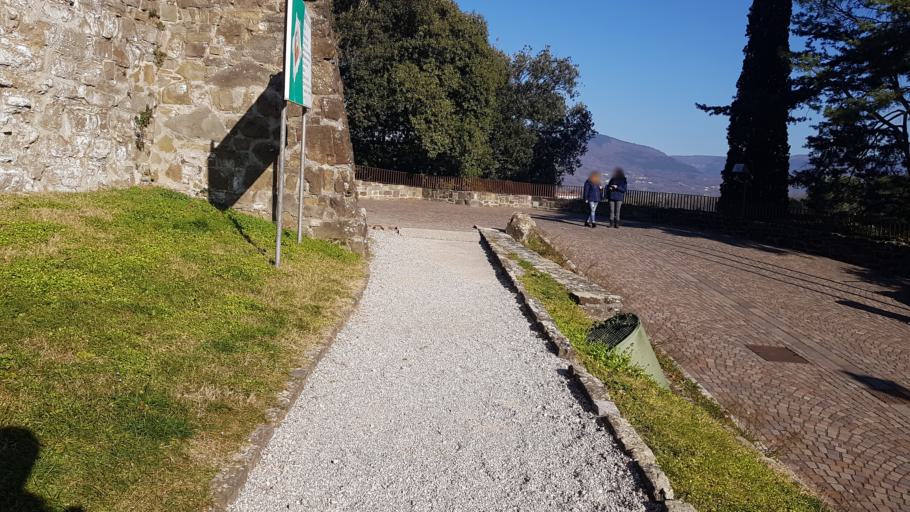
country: IT
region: Friuli Venezia Giulia
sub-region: Provincia di Gorizia
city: Gorizia
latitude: 45.9441
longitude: 13.6281
